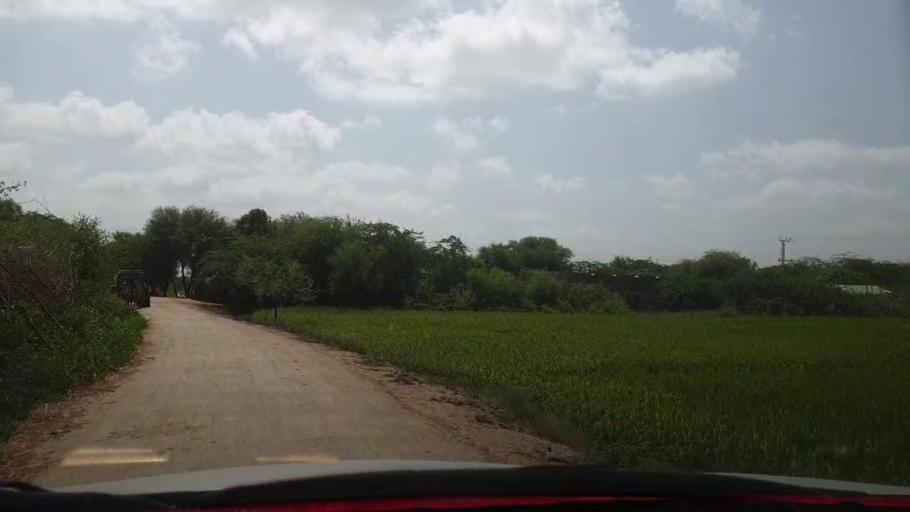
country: PK
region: Sindh
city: Talhar
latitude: 24.9073
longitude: 68.8462
